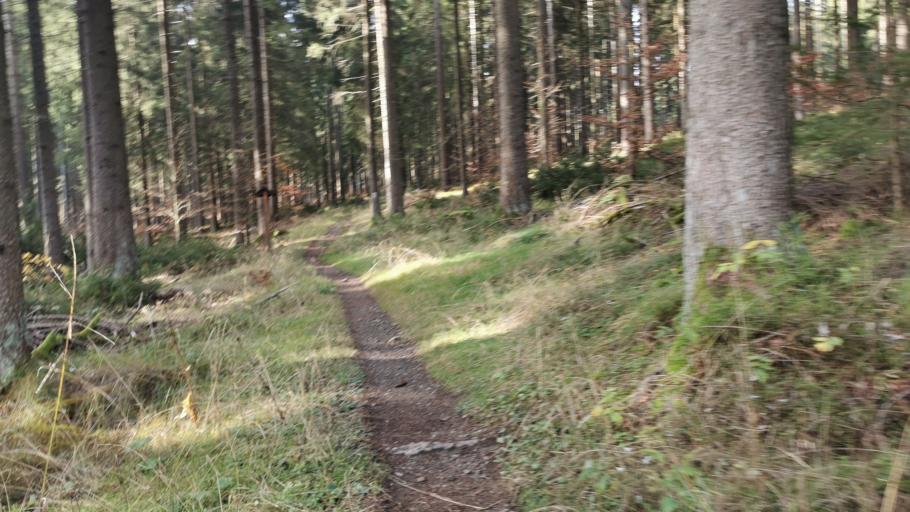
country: DE
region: Bavaria
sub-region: Upper Franconia
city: Tschirn
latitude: 50.4417
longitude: 11.4532
